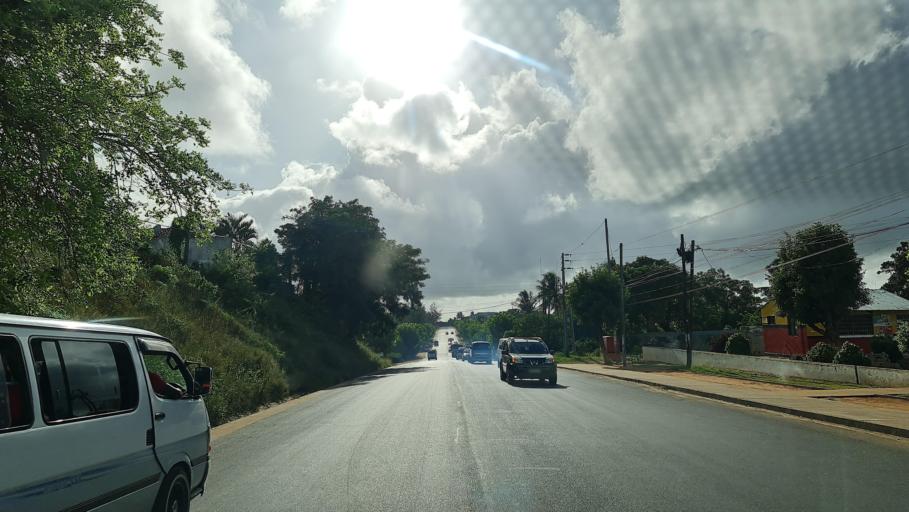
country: MZ
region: Gaza
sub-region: Xai-Xai District
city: Xai-Xai
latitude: -25.0568
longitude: 33.6559
